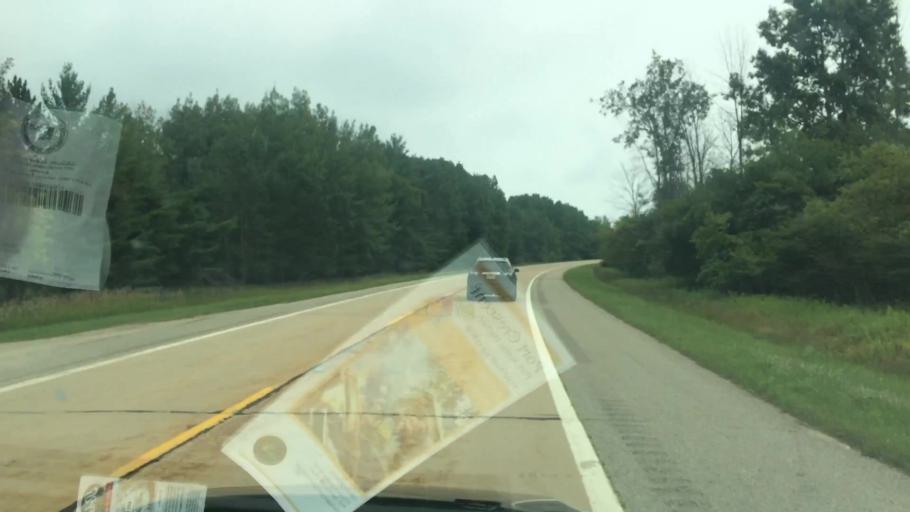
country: US
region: Michigan
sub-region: Huron County
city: Harbor Beach
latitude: 44.0272
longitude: -82.8259
